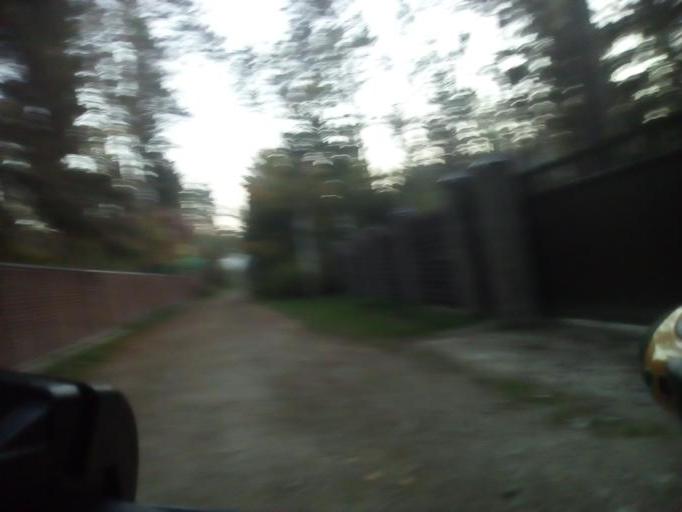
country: RU
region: Moskovskaya
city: Kratovo
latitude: 55.6016
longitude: 38.1590
